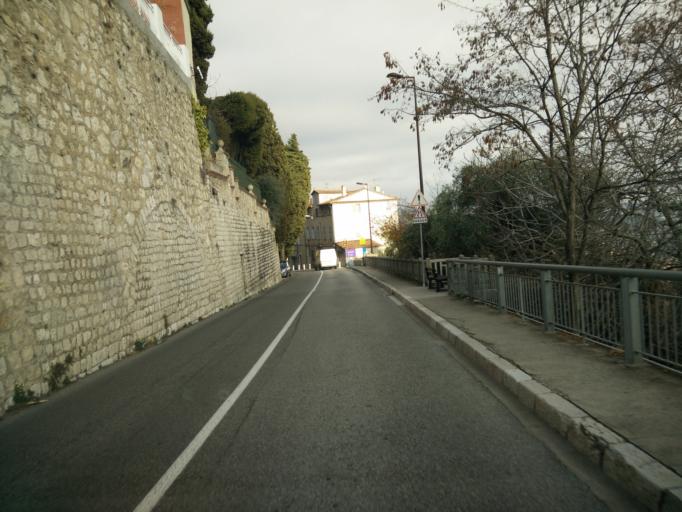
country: FR
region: Provence-Alpes-Cote d'Azur
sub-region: Departement des Alpes-Maritimes
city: Grasse
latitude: 43.6572
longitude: 6.9179
